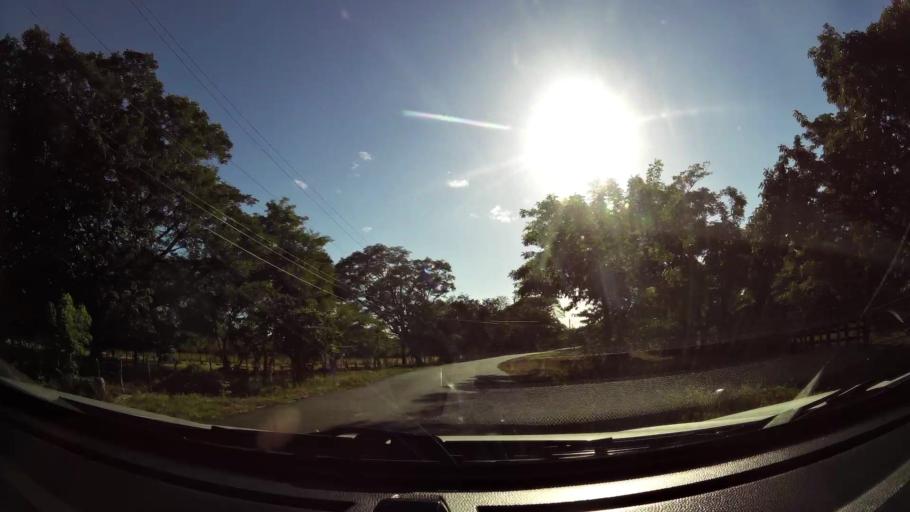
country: CR
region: Guanacaste
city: Sardinal
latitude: 10.4898
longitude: -85.6263
